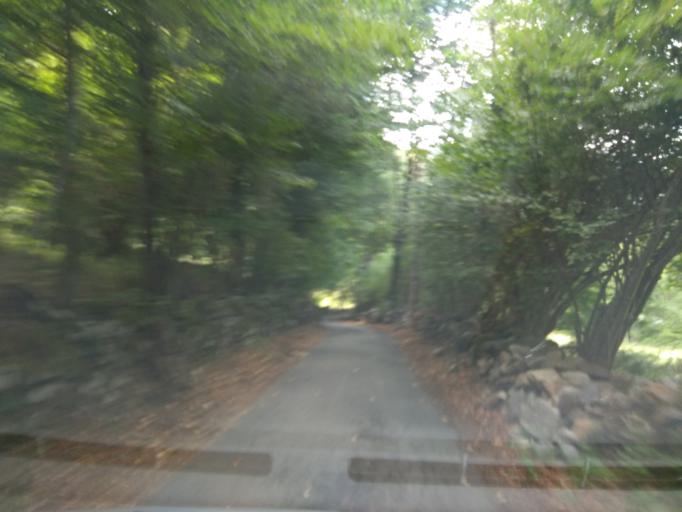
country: ES
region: Catalonia
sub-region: Provincia de Lleida
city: Les
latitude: 42.7540
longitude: 0.6947
